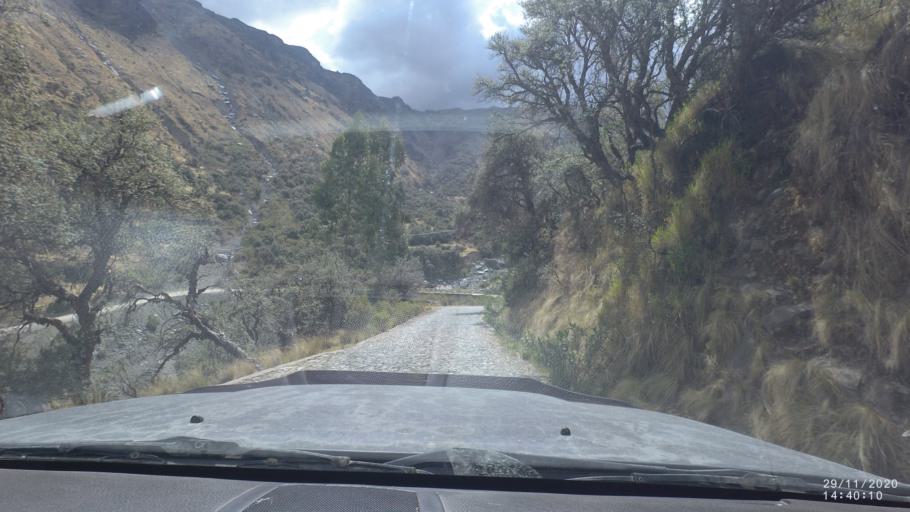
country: BO
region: Cochabamba
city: Sipe Sipe
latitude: -17.2749
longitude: -66.3293
